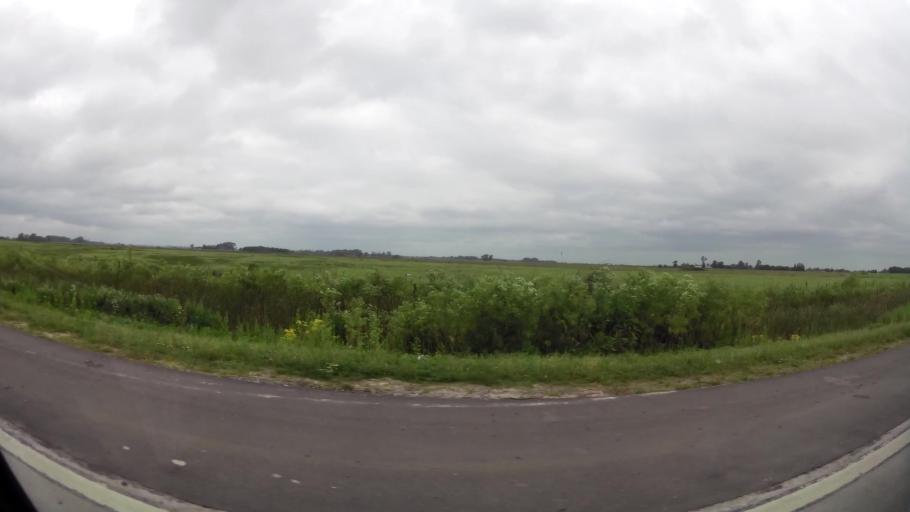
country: AR
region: Buenos Aires
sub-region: Partido de San Vicente
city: San Vicente
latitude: -35.0218
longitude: -58.3200
